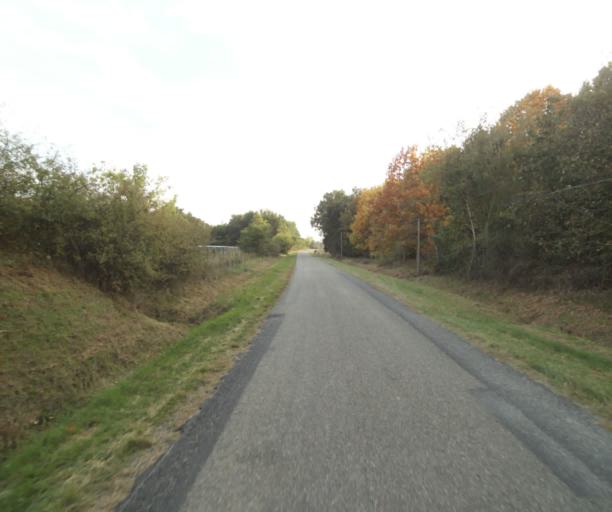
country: FR
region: Midi-Pyrenees
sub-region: Departement du Tarn-et-Garonne
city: Campsas
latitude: 43.8799
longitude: 1.3209
